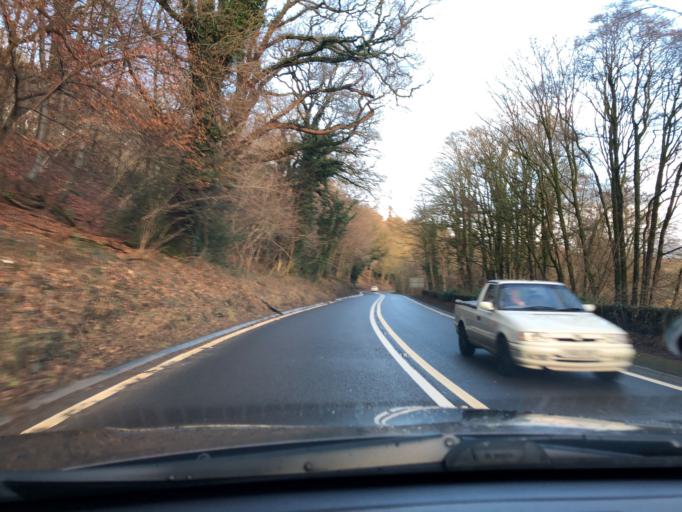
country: GB
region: England
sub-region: Cumbria
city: Ulverston
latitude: 54.2425
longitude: -3.0482
